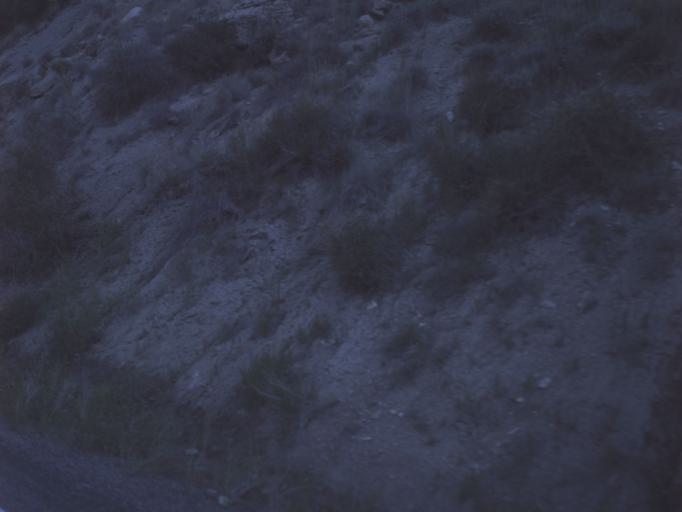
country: US
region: Utah
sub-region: Emery County
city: Huntington
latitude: 39.4250
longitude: -111.1271
